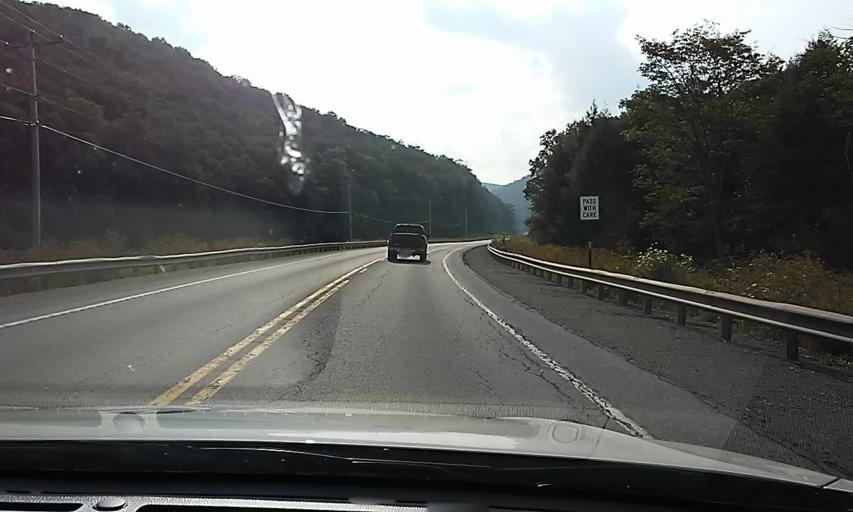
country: US
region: Pennsylvania
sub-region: Potter County
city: Galeton
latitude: 41.7806
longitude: -77.8075
